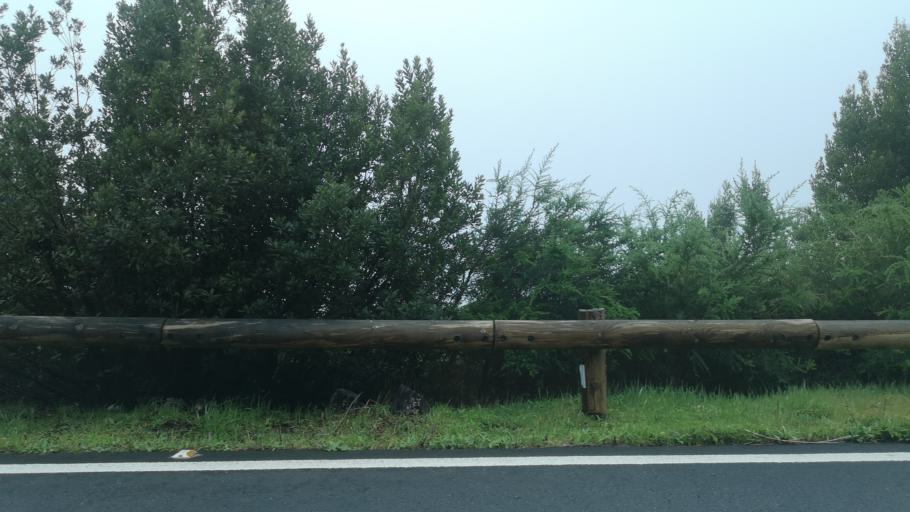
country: ES
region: Canary Islands
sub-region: Provincia de Santa Cruz de Tenerife
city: Vallehermosa
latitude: 28.1290
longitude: -17.2747
